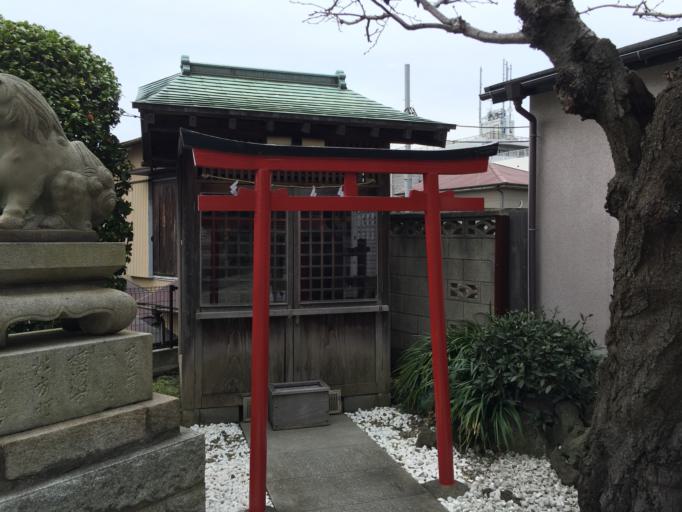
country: JP
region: Kanagawa
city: Yokohama
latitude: 35.4316
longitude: 139.6535
